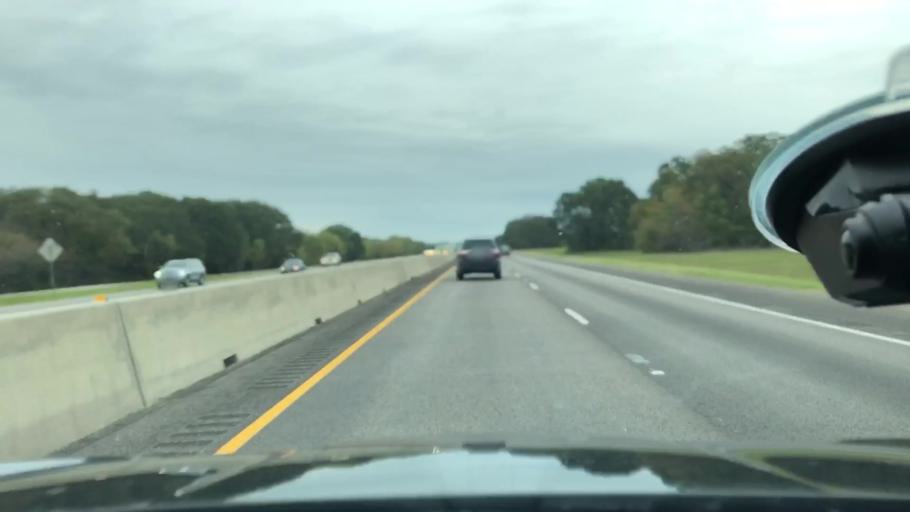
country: US
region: Texas
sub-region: Franklin County
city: Mount Vernon
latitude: 33.1660
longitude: -95.3782
